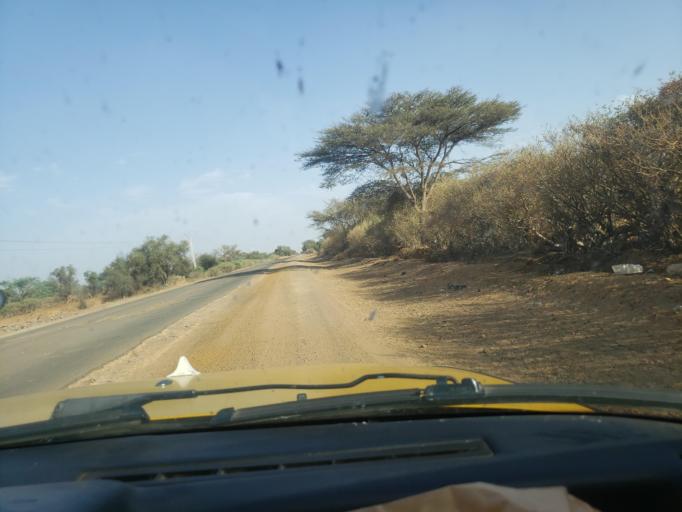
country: SN
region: Louga
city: Louga
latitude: 15.5093
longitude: -15.9784
